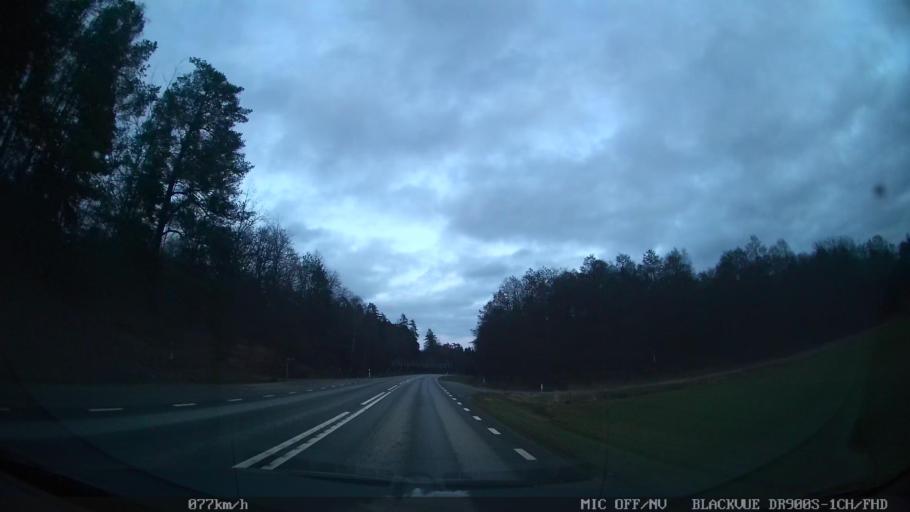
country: SE
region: Skane
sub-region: Hassleholms Kommun
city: Bjarnum
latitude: 56.2059
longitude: 13.6419
